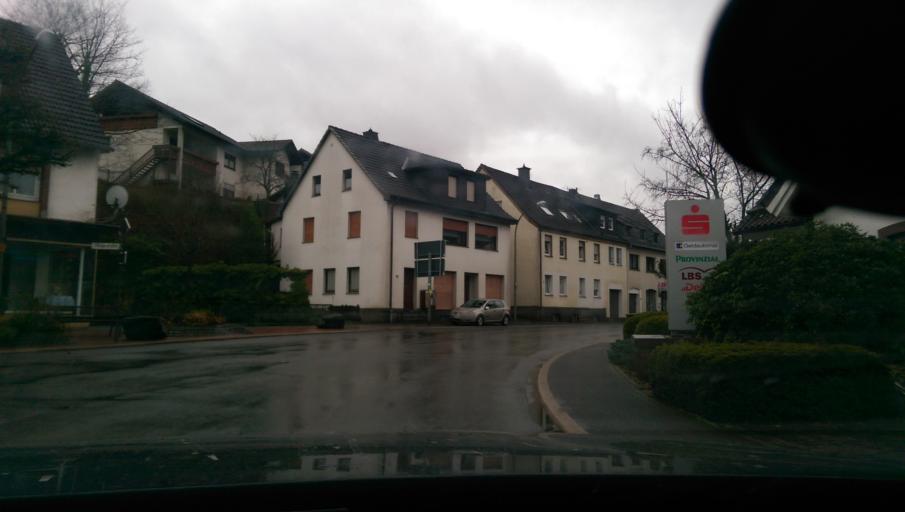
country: DE
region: North Rhine-Westphalia
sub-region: Regierungsbezirk Arnsberg
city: Finnentrop
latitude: 51.2182
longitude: 7.9576
